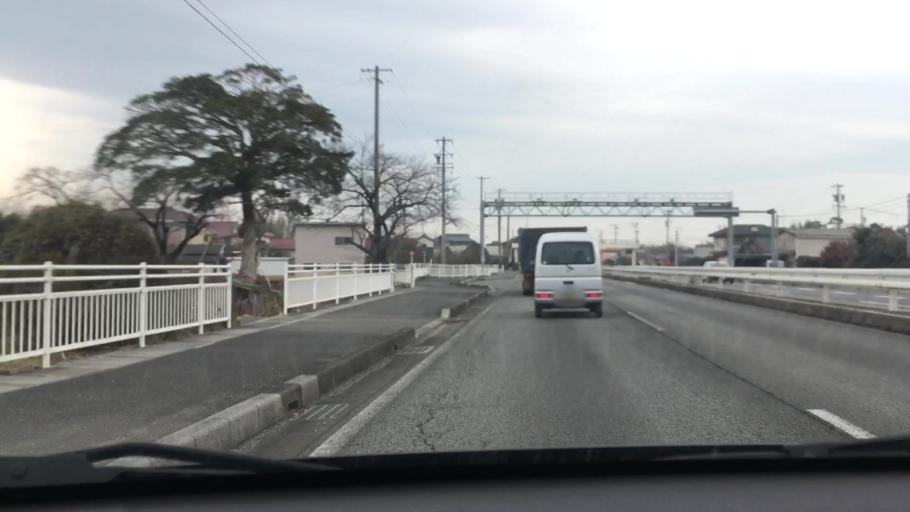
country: JP
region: Mie
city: Suzuka
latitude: 34.9038
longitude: 136.5490
